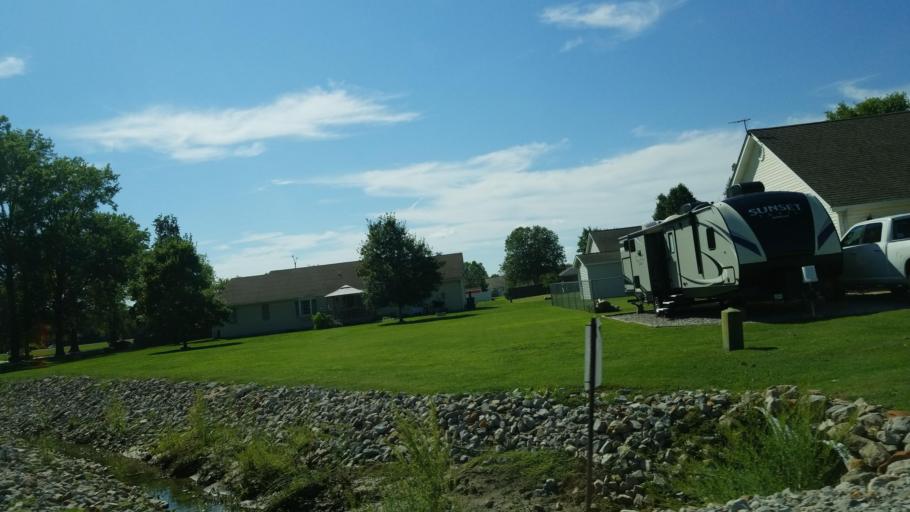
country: US
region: Illinois
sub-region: Williamson County
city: Marion
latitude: 37.7412
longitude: -88.9015
